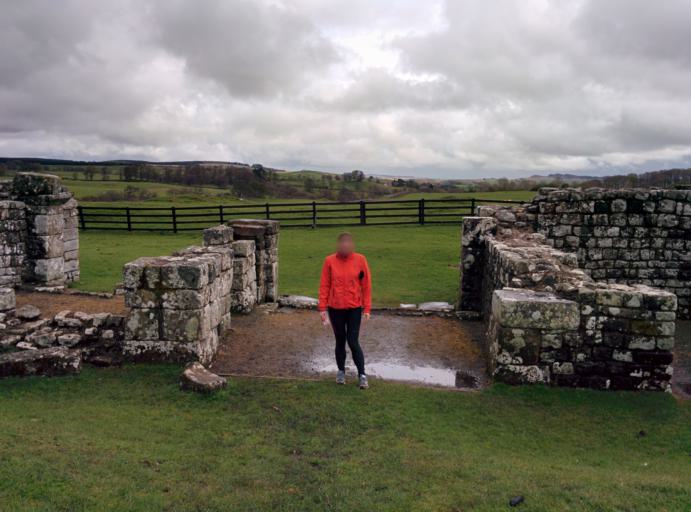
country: GB
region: England
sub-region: Northumberland
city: Greenhead
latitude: 54.9898
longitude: -2.6018
